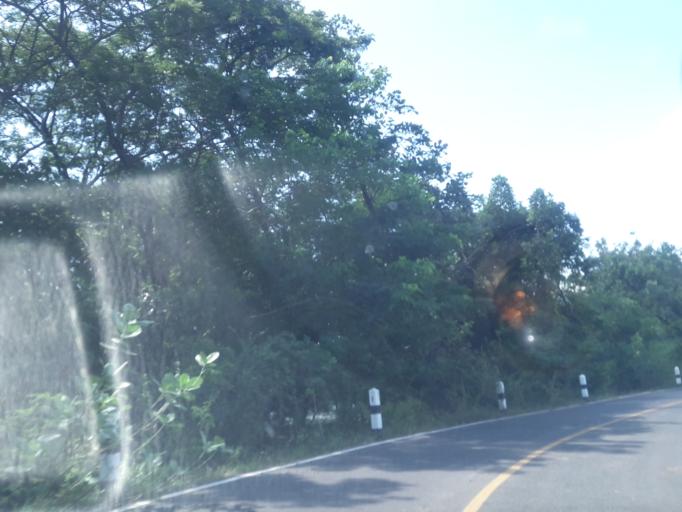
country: TH
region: Lop Buri
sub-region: Amphoe Tha Luang
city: Tha Luang
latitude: 15.0527
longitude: 101.0290
